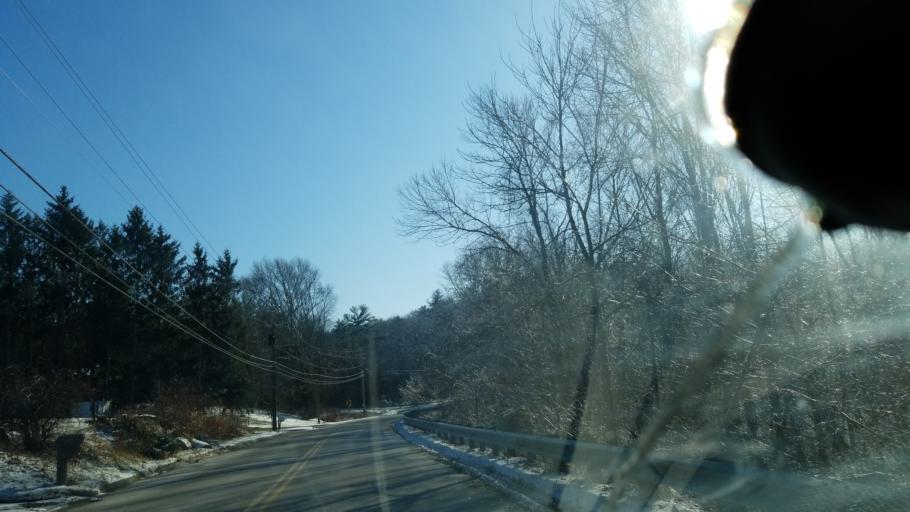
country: US
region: Connecticut
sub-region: Windham County
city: Danielson
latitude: 41.7896
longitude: -71.8795
